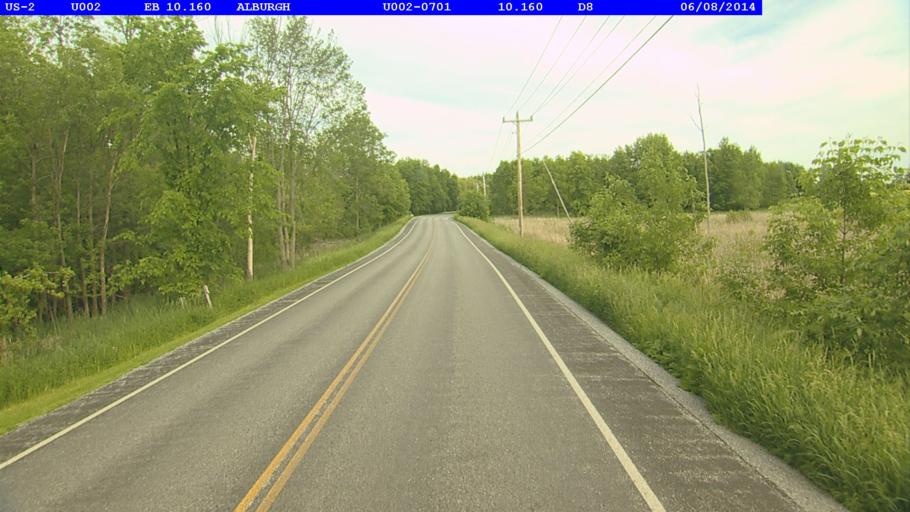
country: US
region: Vermont
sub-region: Grand Isle County
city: North Hero
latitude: 44.9055
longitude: -73.2767
